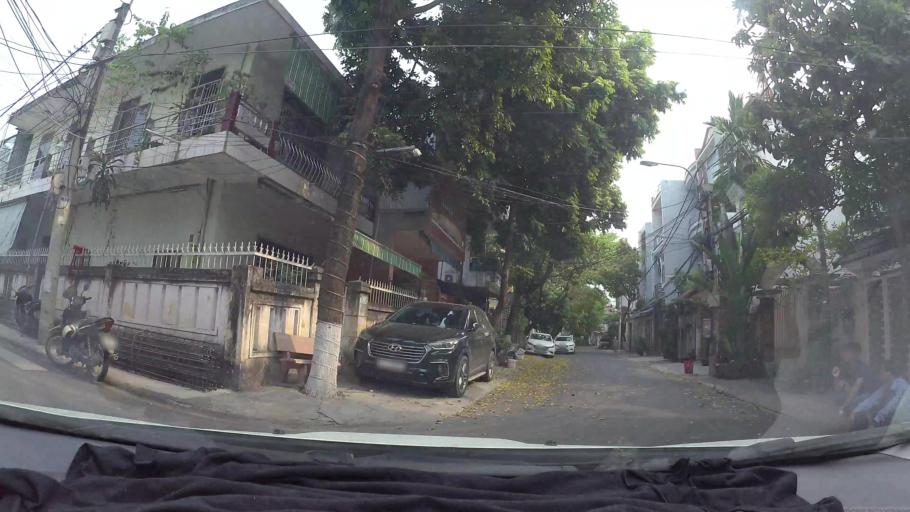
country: VN
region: Da Nang
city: Son Tra
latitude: 16.0443
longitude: 108.2193
